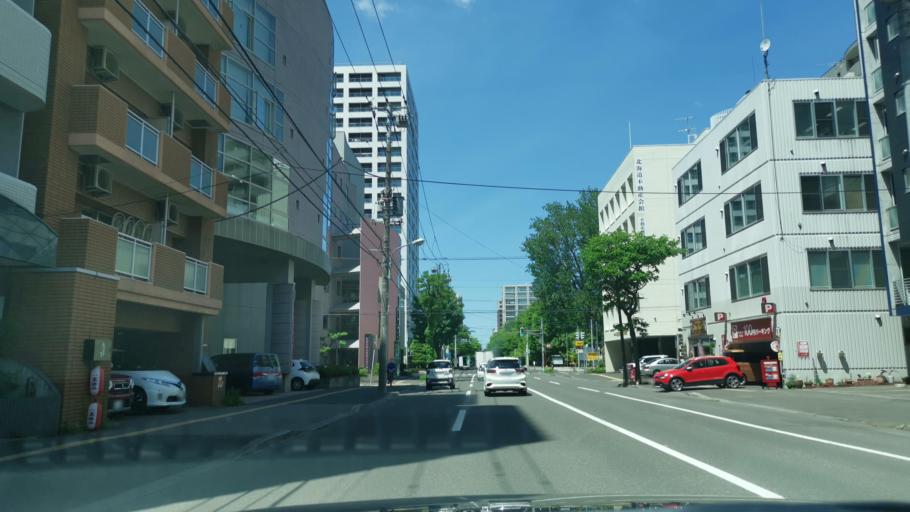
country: JP
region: Hokkaido
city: Sapporo
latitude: 43.0581
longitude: 141.3301
